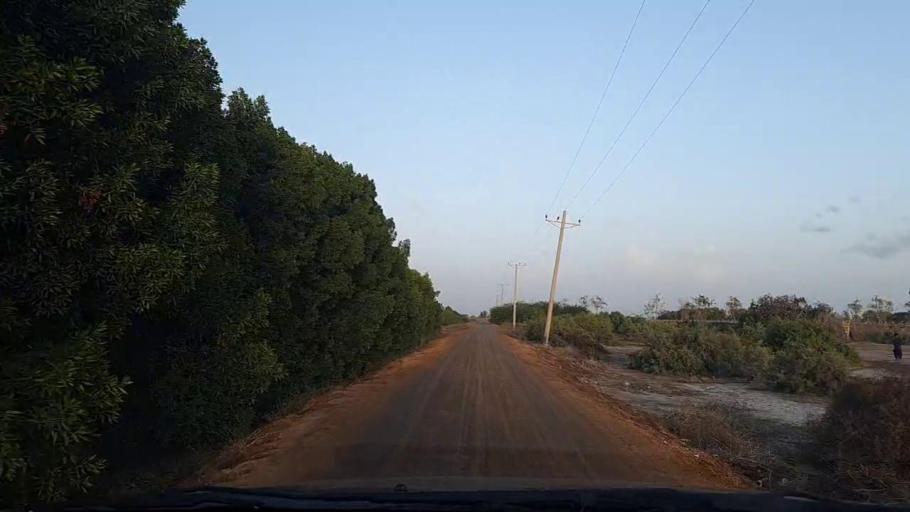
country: PK
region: Sindh
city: Keti Bandar
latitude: 24.1627
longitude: 67.6092
